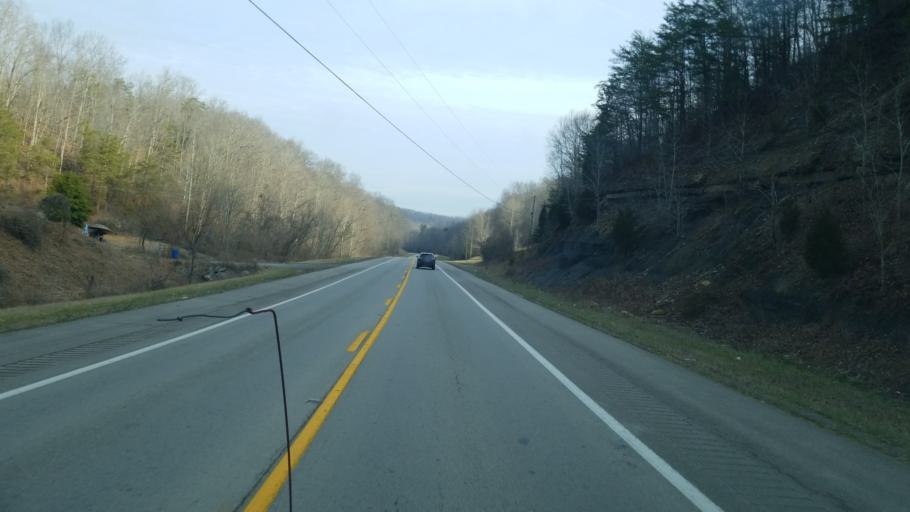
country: US
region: Kentucky
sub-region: Russell County
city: Russell Springs
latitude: 37.1495
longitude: -85.0257
